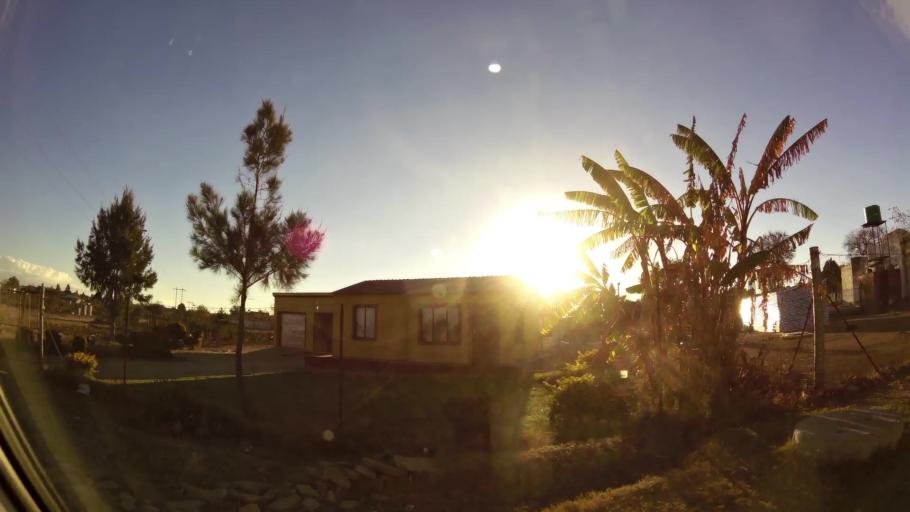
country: ZA
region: Limpopo
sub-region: Capricorn District Municipality
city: Polokwane
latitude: -23.8275
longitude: 29.3767
